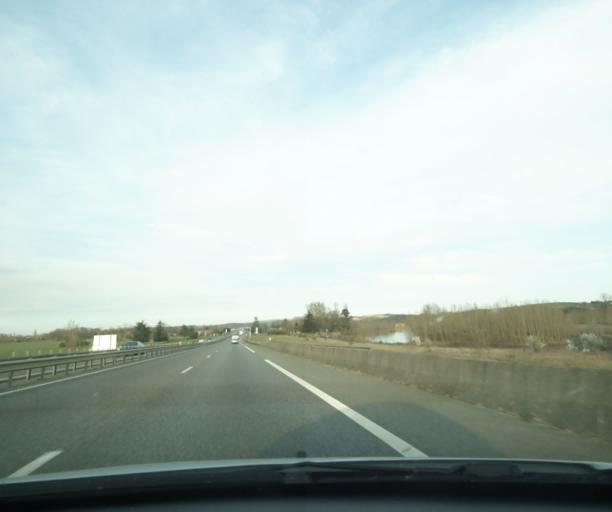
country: FR
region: Midi-Pyrenees
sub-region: Departement de la Haute-Garonne
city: Marquefave
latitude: 43.3326
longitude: 1.2396
